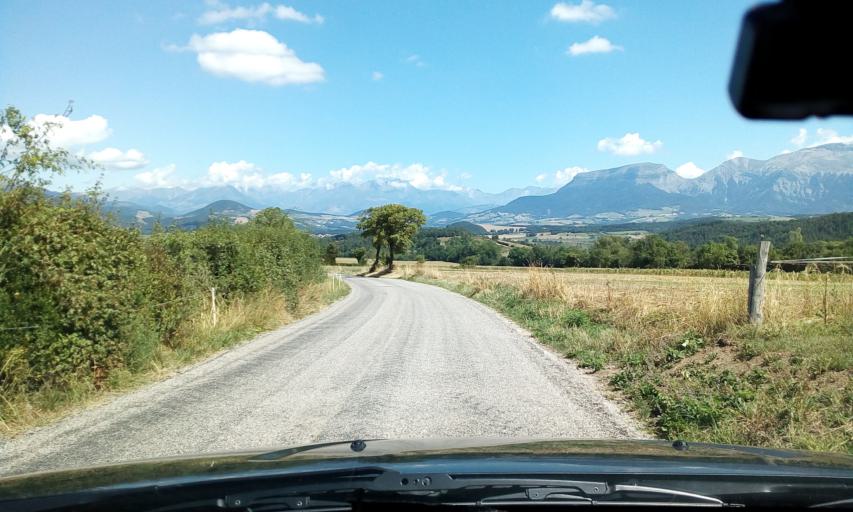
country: FR
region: Rhone-Alpes
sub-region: Departement de l'Isere
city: Mens
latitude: 44.7669
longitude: 5.6653
